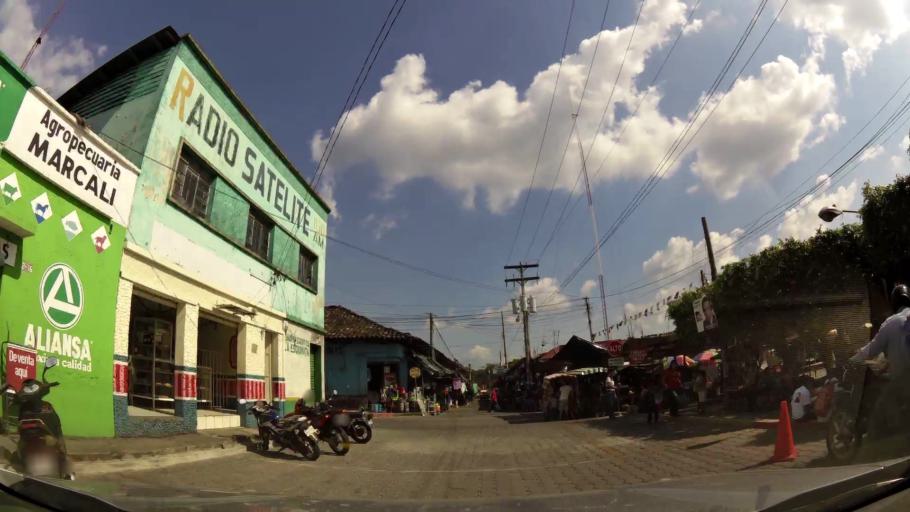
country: GT
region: Suchitepeque
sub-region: Municipio de Cuyotenango
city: Cuyotenango
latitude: 14.5394
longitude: -91.5717
